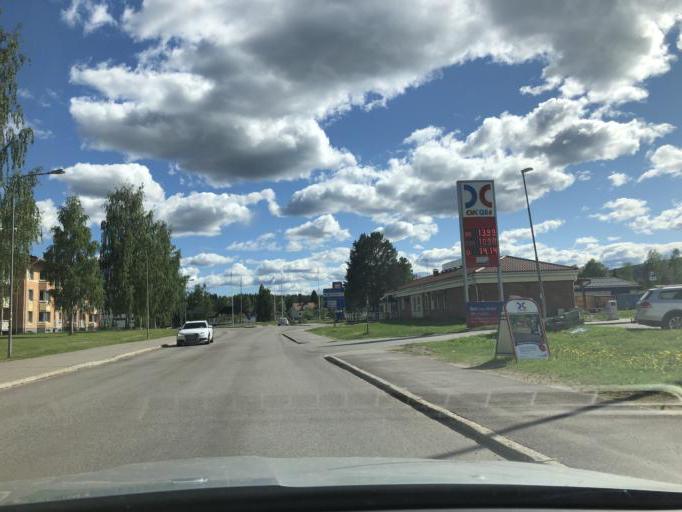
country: SE
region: Norrbotten
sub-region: Alvsbyns Kommun
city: AElvsbyn
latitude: 65.6730
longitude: 21.0060
